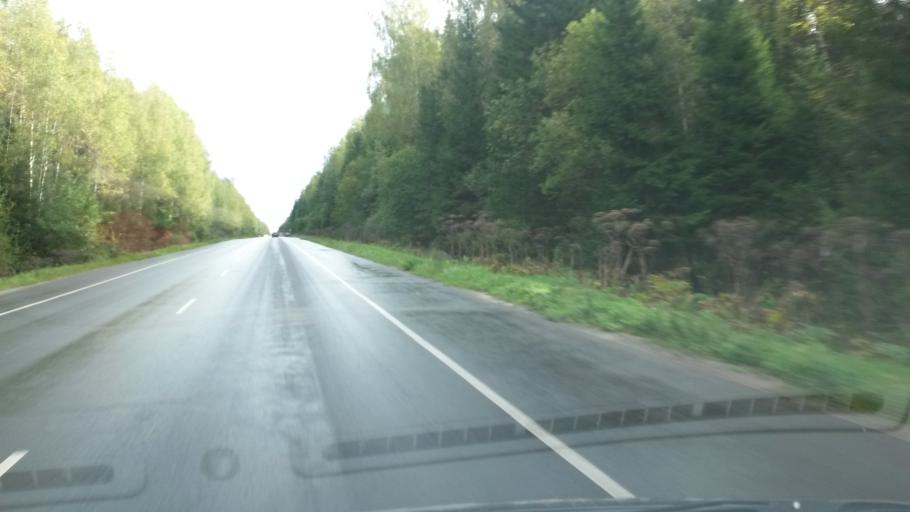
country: RU
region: Ivanovo
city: Kitovo
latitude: 57.0357
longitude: 41.3219
